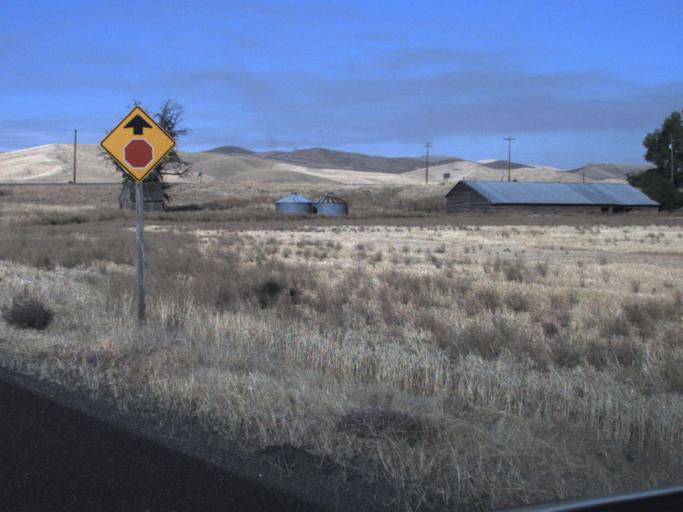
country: US
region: Washington
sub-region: Walla Walla County
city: Waitsburg
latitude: 46.2969
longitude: -118.3408
